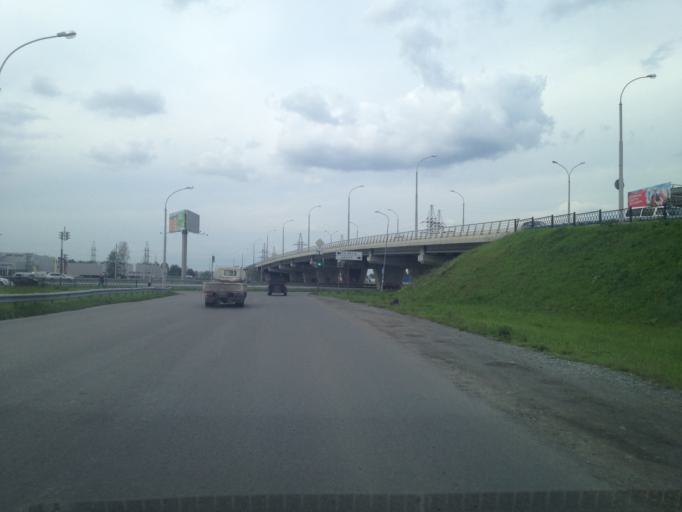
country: RU
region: Sverdlovsk
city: Shirokaya Rechka
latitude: 56.8254
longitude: 60.5130
